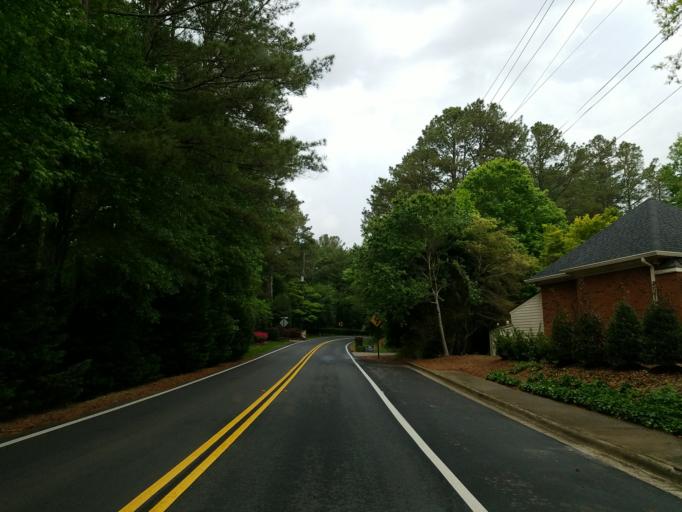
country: US
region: Georgia
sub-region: Fulton County
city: Roswell
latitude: 34.0001
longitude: -84.4458
